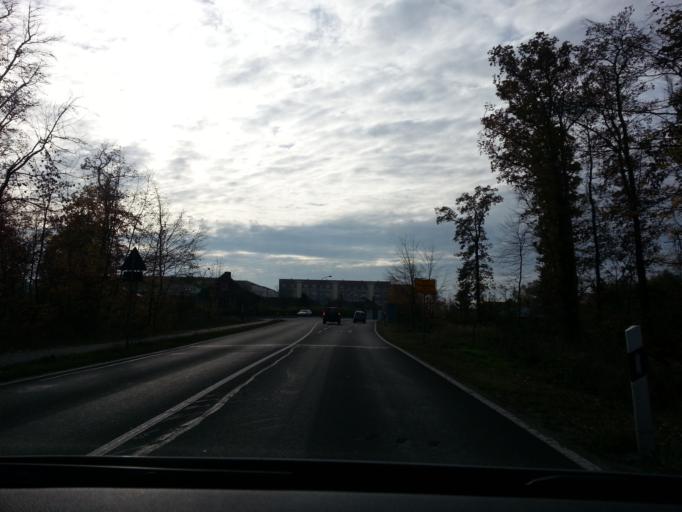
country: DE
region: Mecklenburg-Vorpommern
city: Torgelow
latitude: 53.6423
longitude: 14.0359
